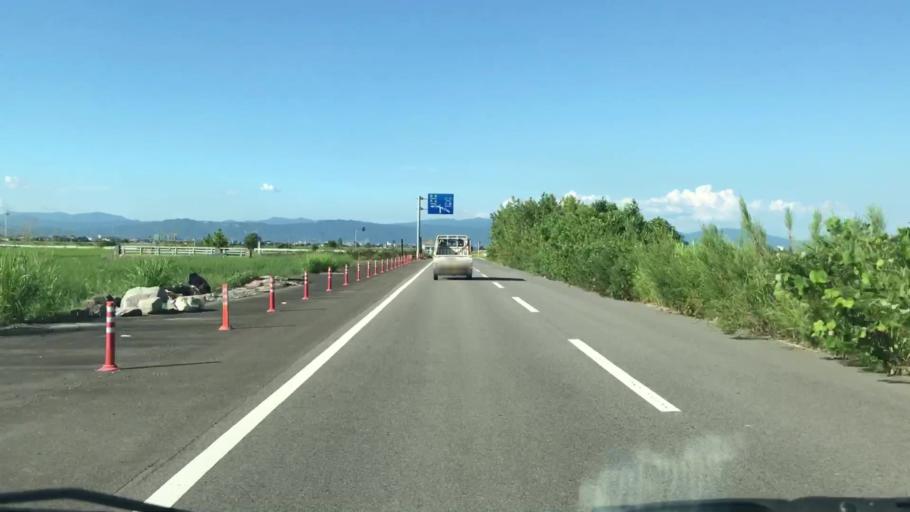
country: JP
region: Saga Prefecture
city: Saga-shi
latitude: 33.2057
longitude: 130.2681
